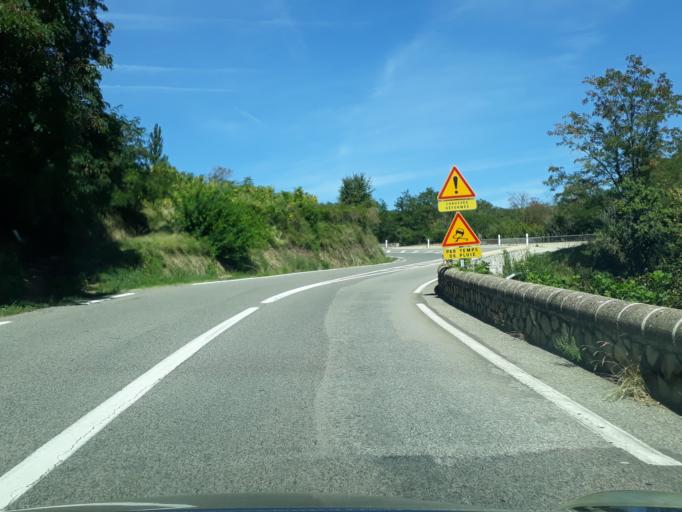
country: FR
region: Rhone-Alpes
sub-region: Departement de l'Ardeche
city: Andance
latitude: 45.2499
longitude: 4.7712
